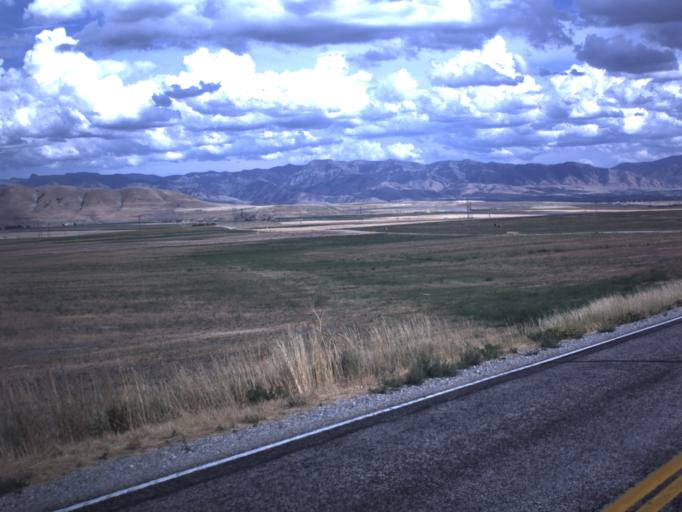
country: US
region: Utah
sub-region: Cache County
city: Benson
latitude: 41.8889
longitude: -112.0375
